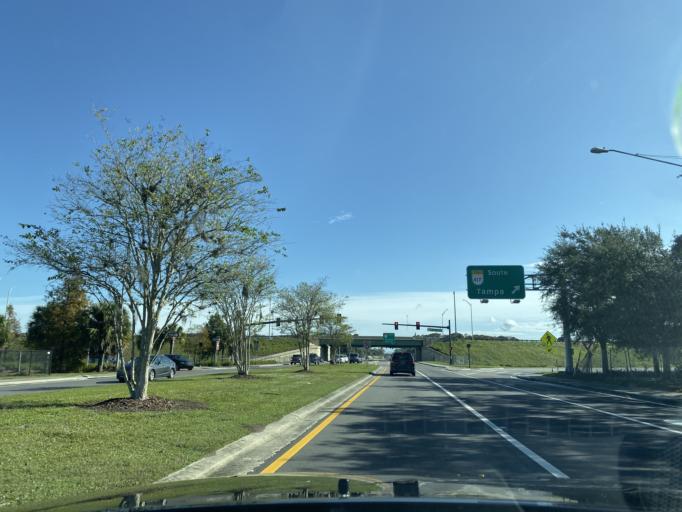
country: US
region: Florida
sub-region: Orange County
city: Azalea Park
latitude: 28.5100
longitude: -81.2498
